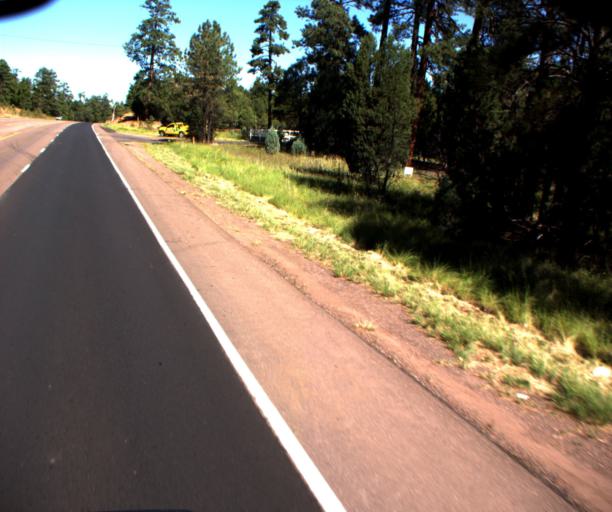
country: US
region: Arizona
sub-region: Navajo County
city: Lake of the Woods
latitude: 34.1776
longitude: -110.0100
